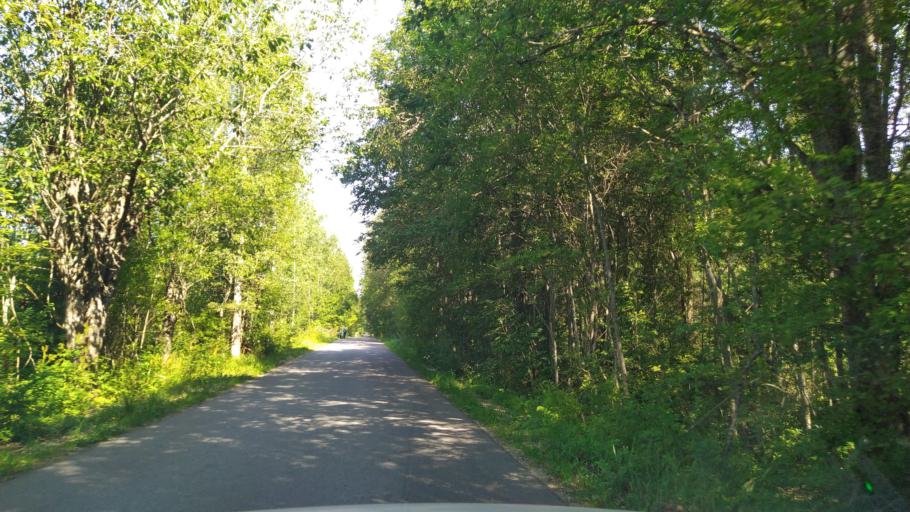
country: RU
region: Leningrad
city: Rozhdestveno
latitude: 59.2684
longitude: 30.0243
